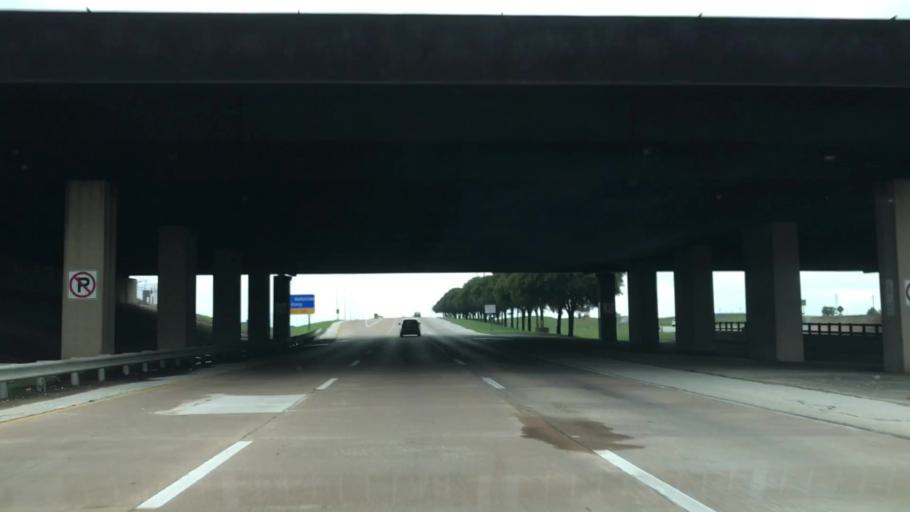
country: US
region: Texas
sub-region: Tarrant County
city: Grapevine
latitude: 32.8854
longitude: -97.0411
